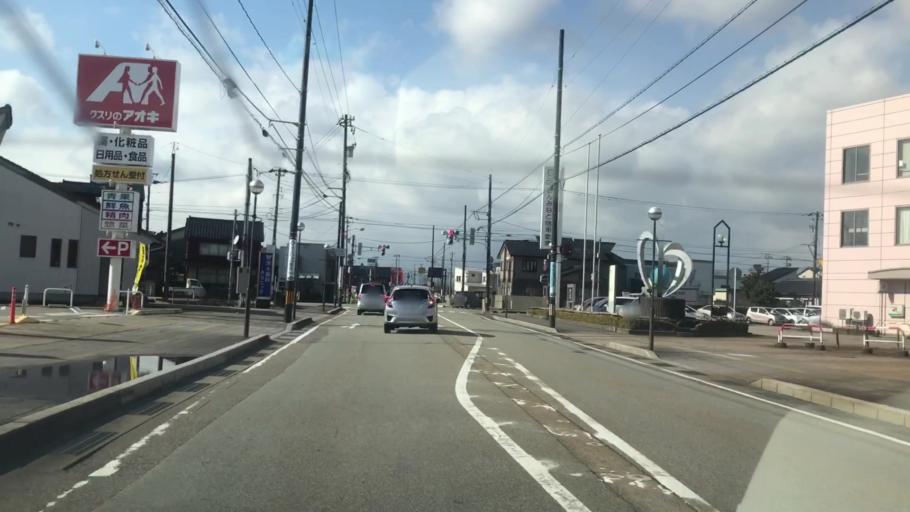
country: JP
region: Toyama
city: Takaoka
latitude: 36.7332
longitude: 137.0496
